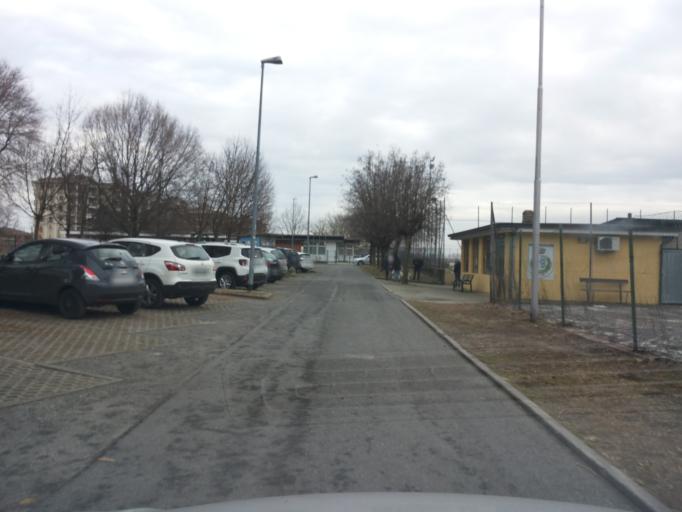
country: IT
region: Piedmont
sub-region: Provincia di Torino
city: Cascinette d'Ivrea
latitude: 45.4760
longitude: 7.9009
